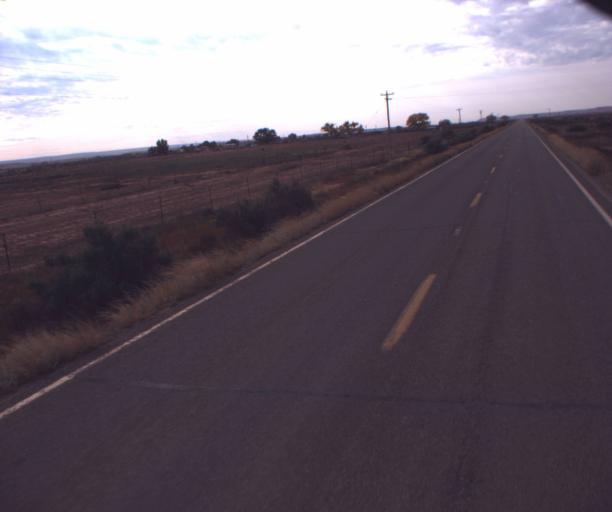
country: US
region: Arizona
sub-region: Apache County
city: Many Farms
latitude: 36.4138
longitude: -109.6072
